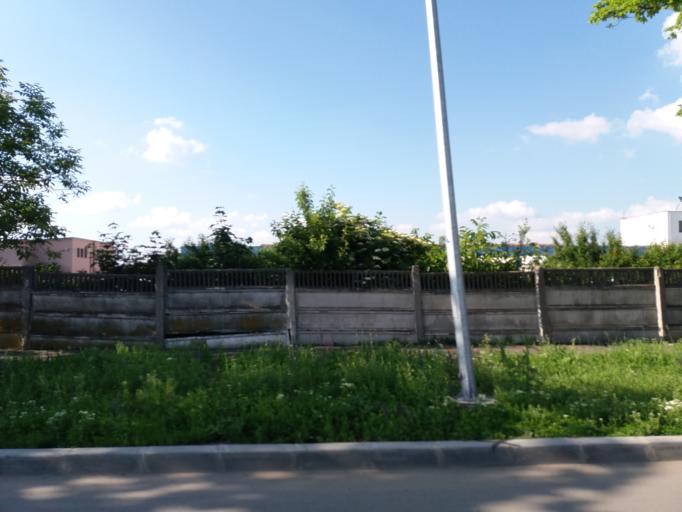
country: RO
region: Arad
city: Arad
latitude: 46.1690
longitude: 21.2830
